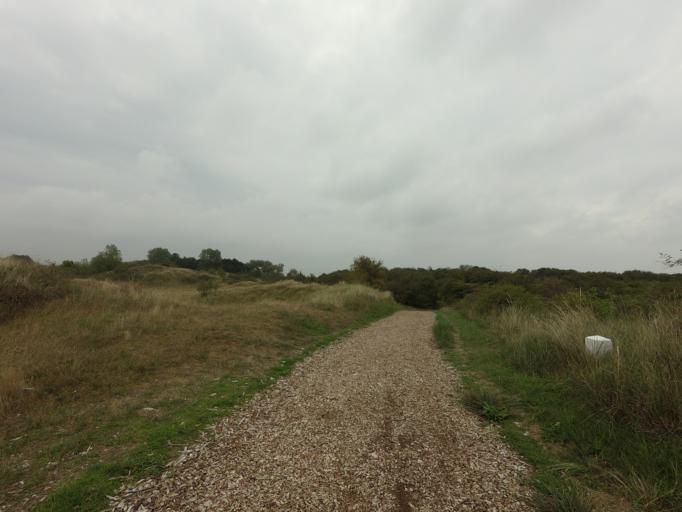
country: NL
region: Friesland
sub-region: Gemeente Schiermonnikoog
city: Schiermonnikoog
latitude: 53.4863
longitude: 6.1830
